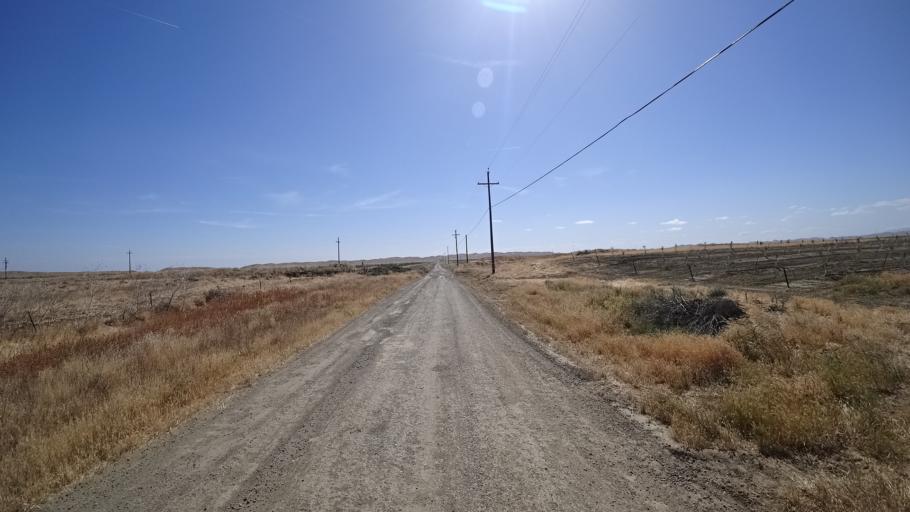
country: US
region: California
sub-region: Kings County
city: Avenal
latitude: 35.8178
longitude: -120.0829
